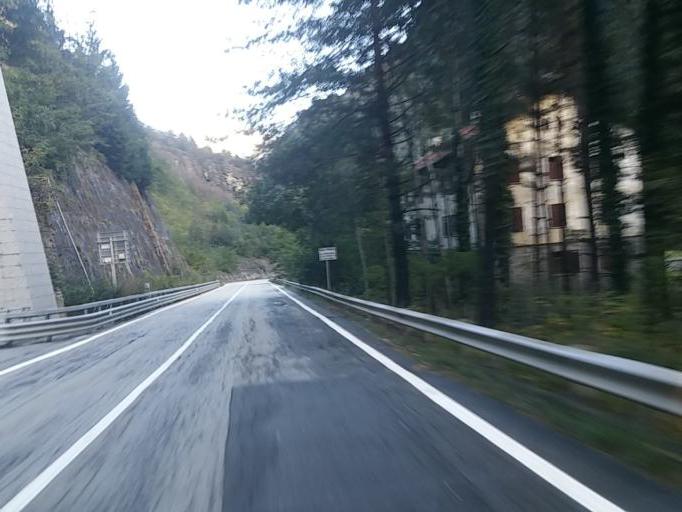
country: IT
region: Piedmont
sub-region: Provincia Verbano-Cusio-Ossola
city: Trasquera
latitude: 46.2067
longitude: 8.2050
